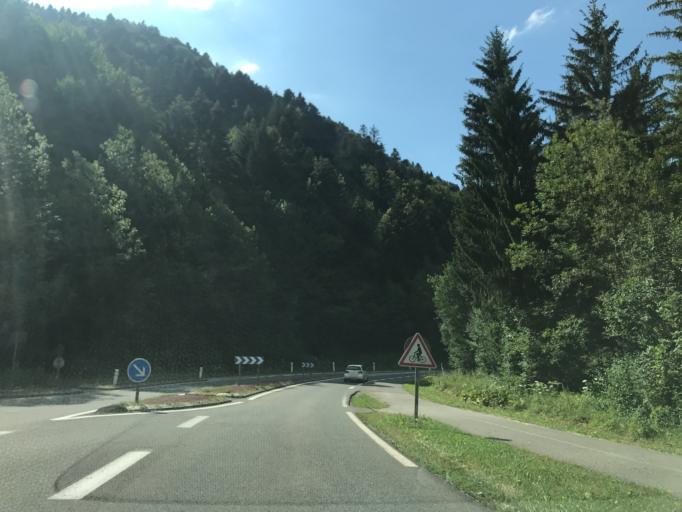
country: FR
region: Rhone-Alpes
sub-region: Departement de la Haute-Savoie
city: Dingy-Saint-Clair
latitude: 45.8989
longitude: 6.2147
